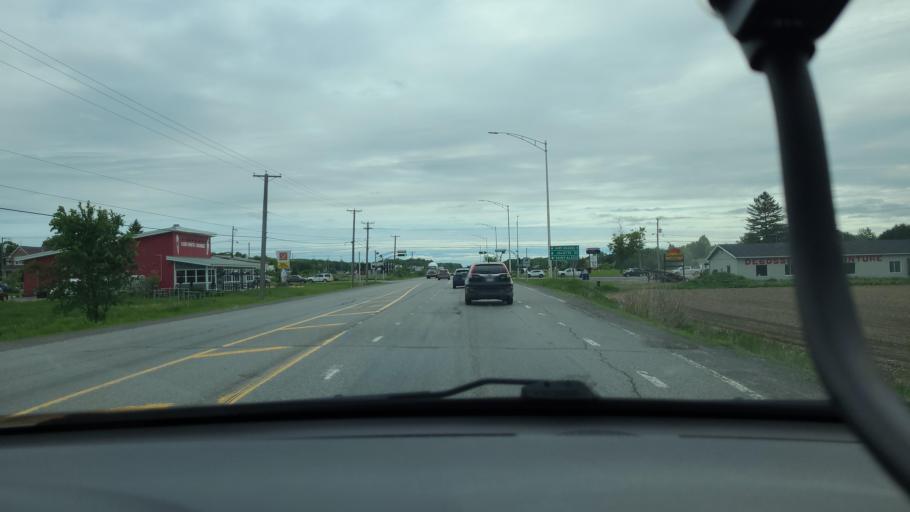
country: CA
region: Quebec
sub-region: Lanaudiere
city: Saint-Jacques
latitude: 45.9308
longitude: -73.6128
